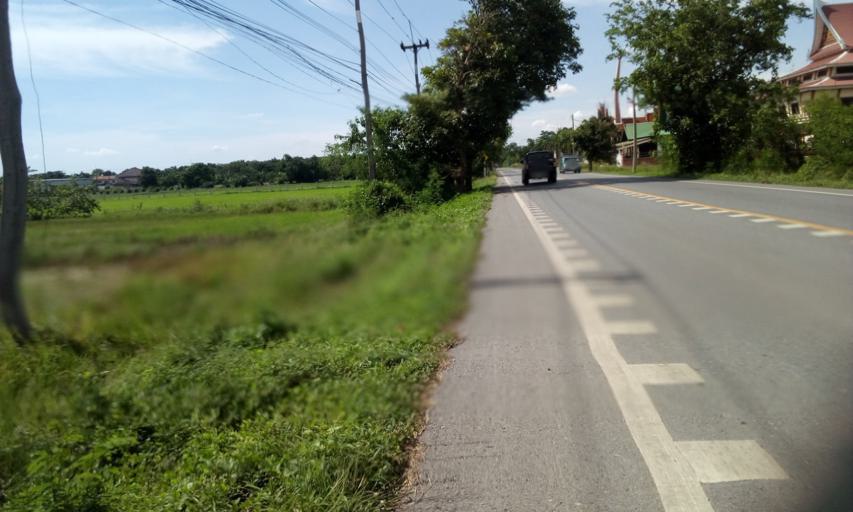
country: TH
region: Pathum Thani
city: Ban Lam Luk Ka
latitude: 14.0174
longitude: 100.8433
